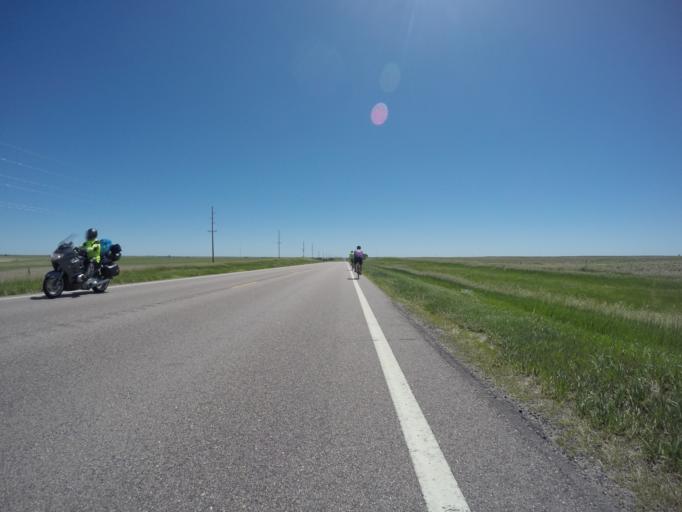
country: US
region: Kansas
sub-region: Norton County
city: Norton
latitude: 39.8284
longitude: -99.6348
